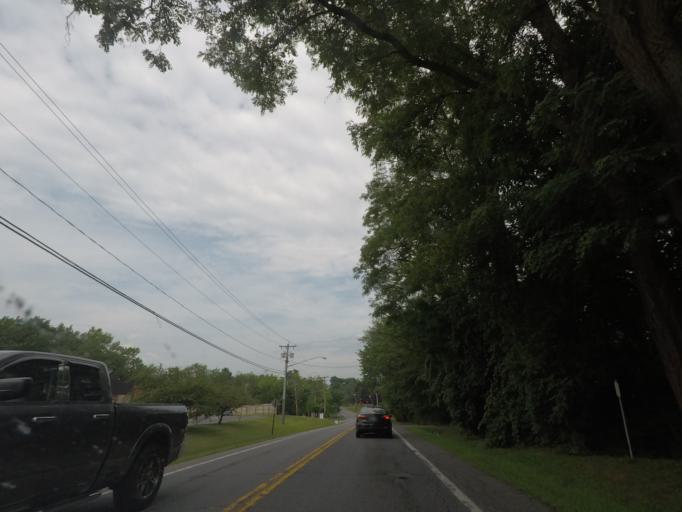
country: US
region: New York
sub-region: Saratoga County
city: Waterford
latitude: 42.8249
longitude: -73.7074
